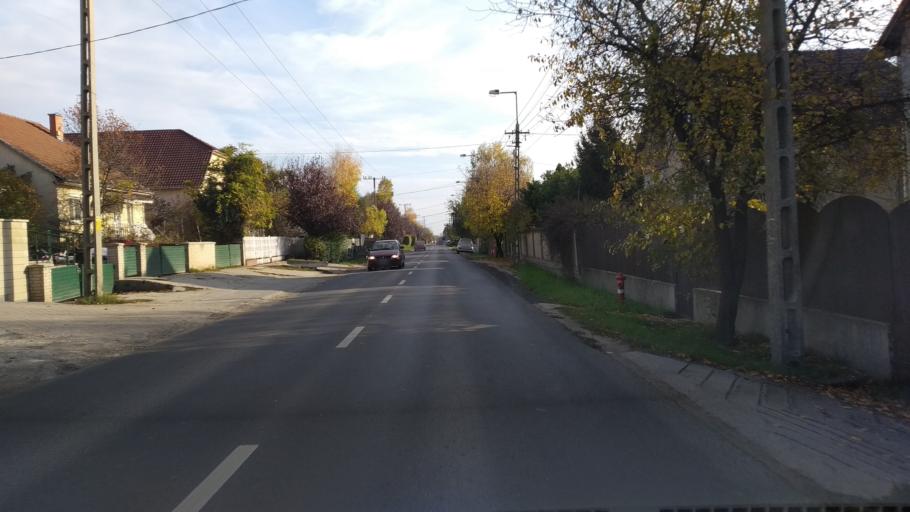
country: HU
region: Pest
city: Maglod
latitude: 47.4462
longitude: 19.3651
